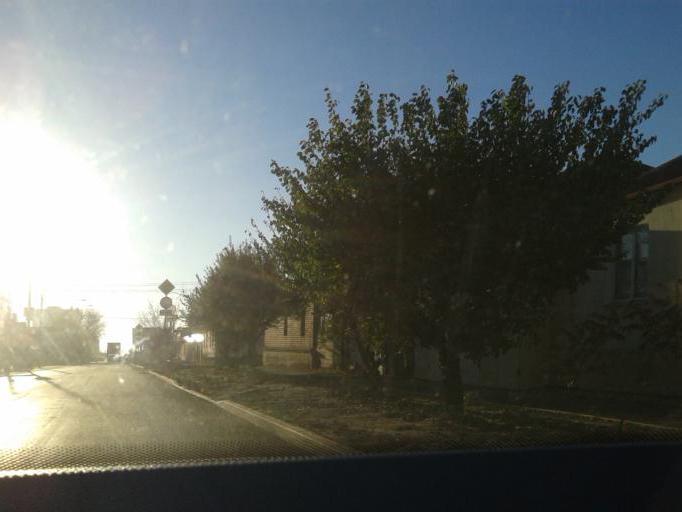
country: RU
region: Volgograd
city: Volgograd
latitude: 48.6975
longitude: 44.4672
